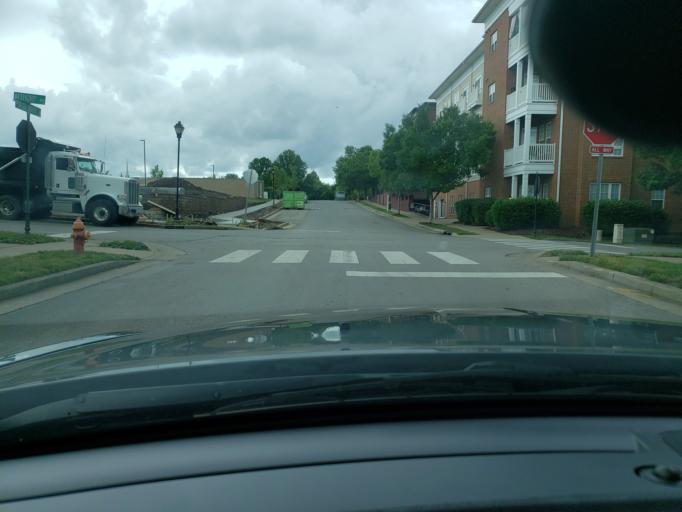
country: US
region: Tennessee
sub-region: Williamson County
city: Brentwood Estates
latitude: 36.0240
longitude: -86.7105
